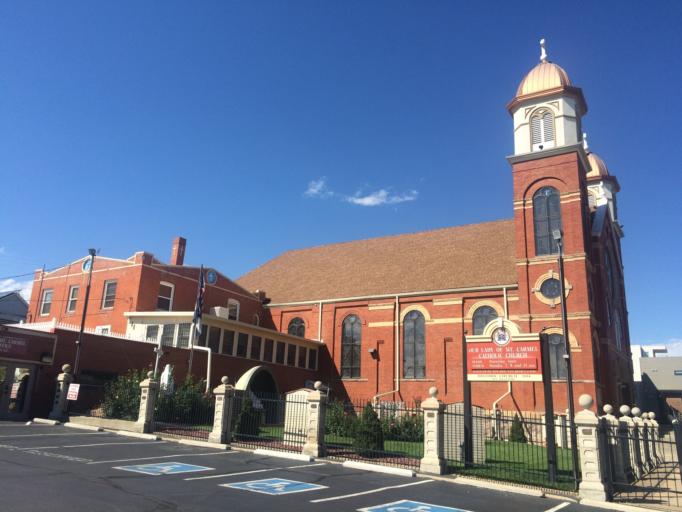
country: US
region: Colorado
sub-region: Denver County
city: Denver
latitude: 39.7664
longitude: -105.0042
